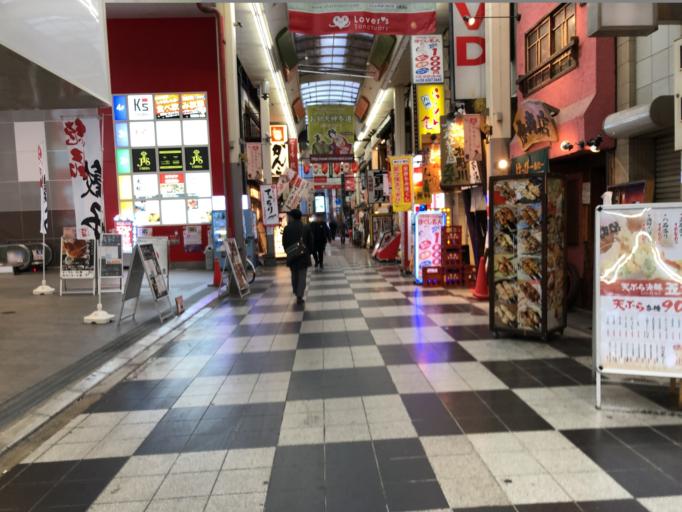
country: JP
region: Osaka
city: Osaka-shi
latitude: 34.7003
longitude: 135.5006
